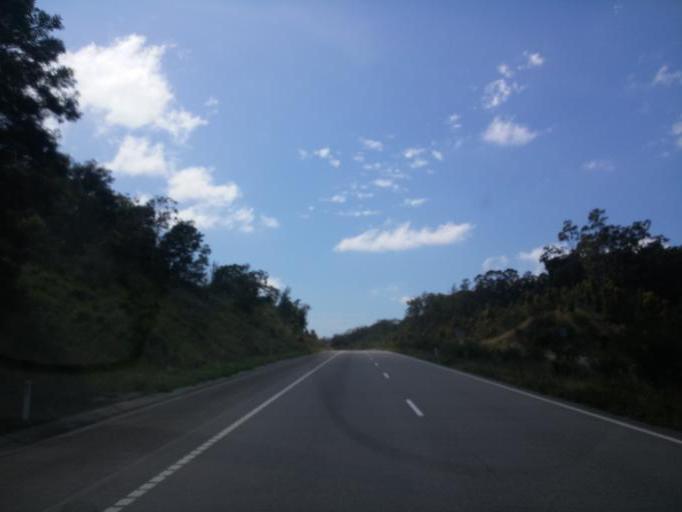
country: AU
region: New South Wales
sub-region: Great Lakes
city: Hawks Nest
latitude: -32.5366
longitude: 152.1738
